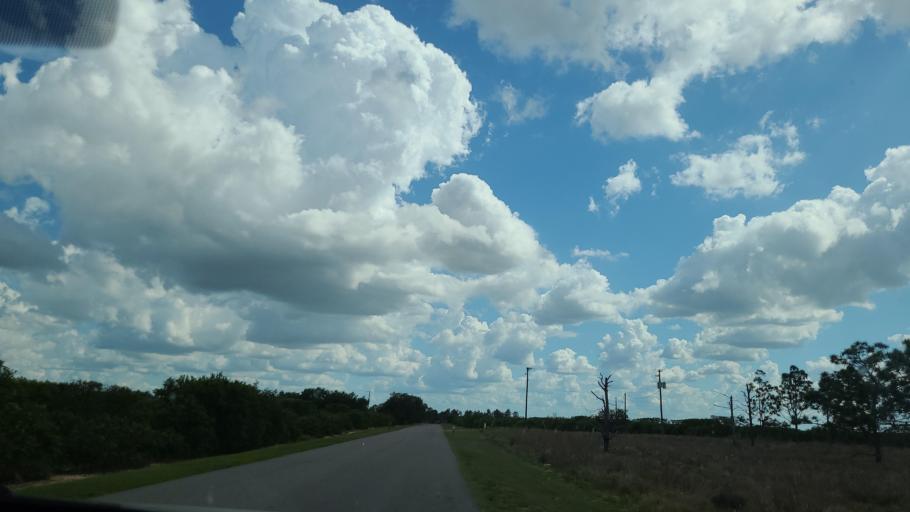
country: US
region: Florida
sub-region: Polk County
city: Lake Wales
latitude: 27.9315
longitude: -81.5696
